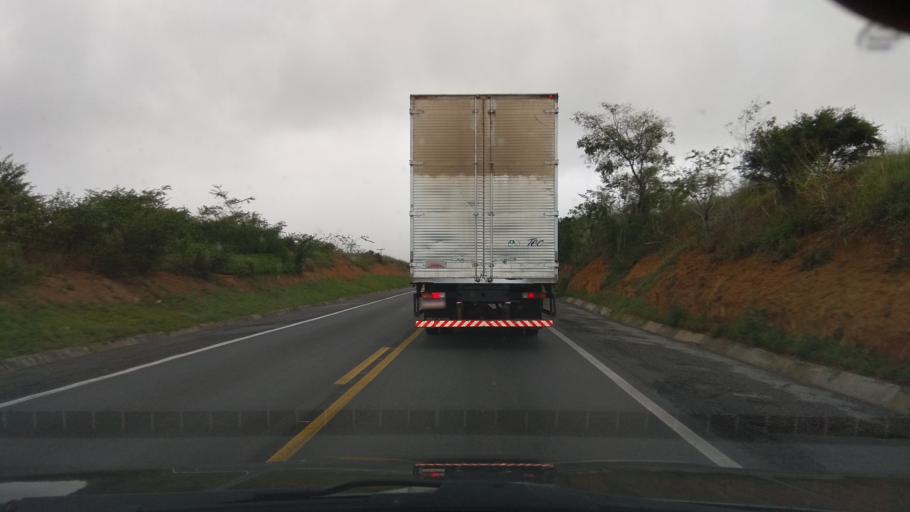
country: BR
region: Bahia
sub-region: Jaguaquara
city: Jaguaquara
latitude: -13.4774
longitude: -40.0408
